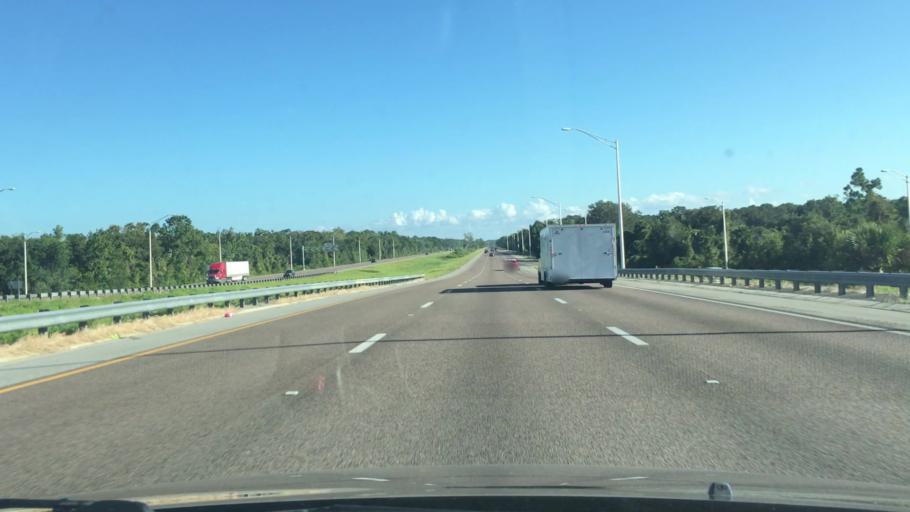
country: US
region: Florida
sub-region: Volusia County
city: Edgewater
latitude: 28.9493
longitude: -80.9503
